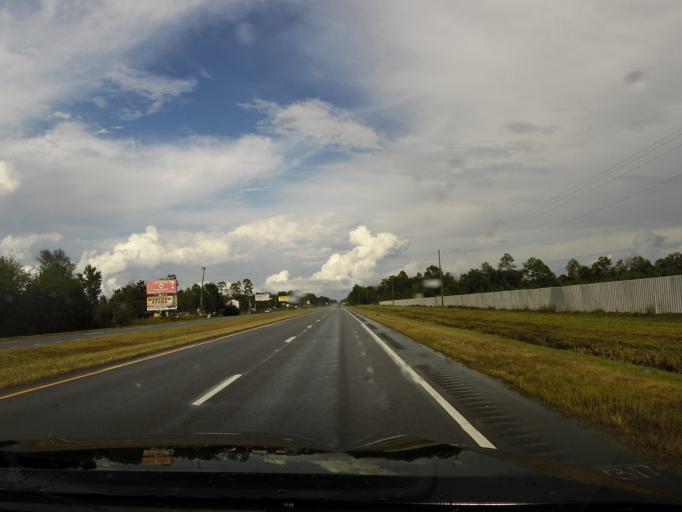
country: US
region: Georgia
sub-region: Liberty County
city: Walthourville
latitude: 31.7664
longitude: -81.6461
